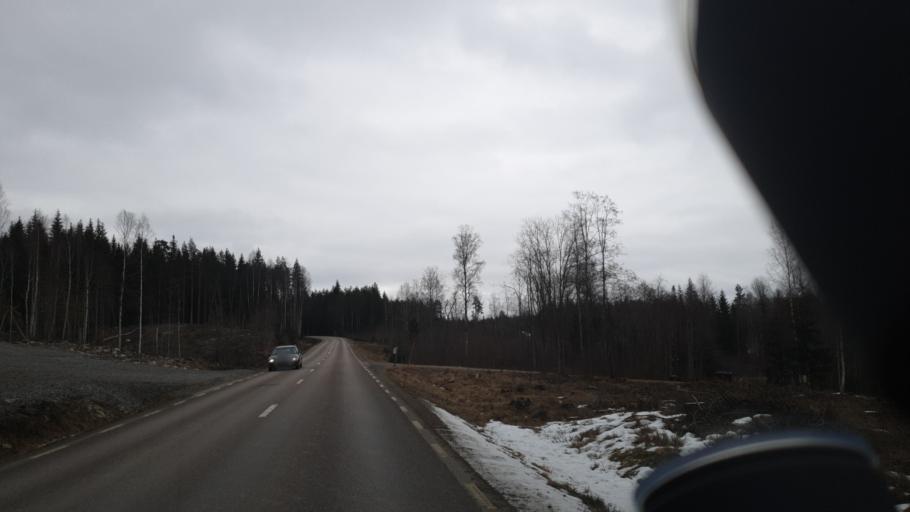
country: SE
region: Vaermland
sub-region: Eda Kommun
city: Amotfors
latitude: 59.6484
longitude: 12.3625
